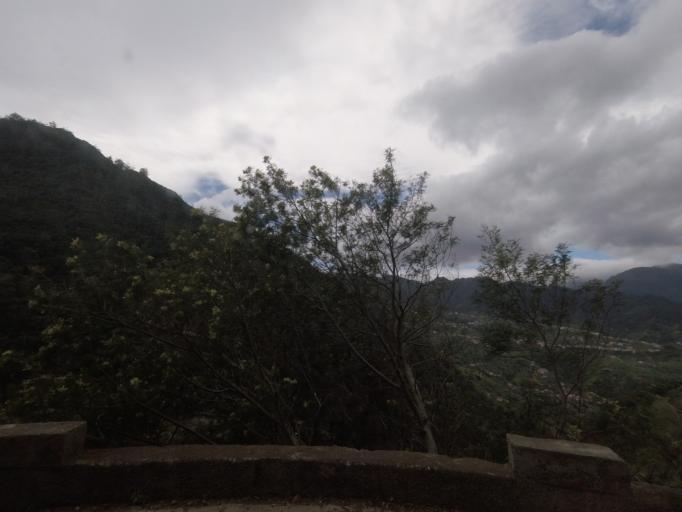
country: PT
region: Madeira
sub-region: Machico
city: Canical
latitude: 32.7633
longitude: -16.8098
